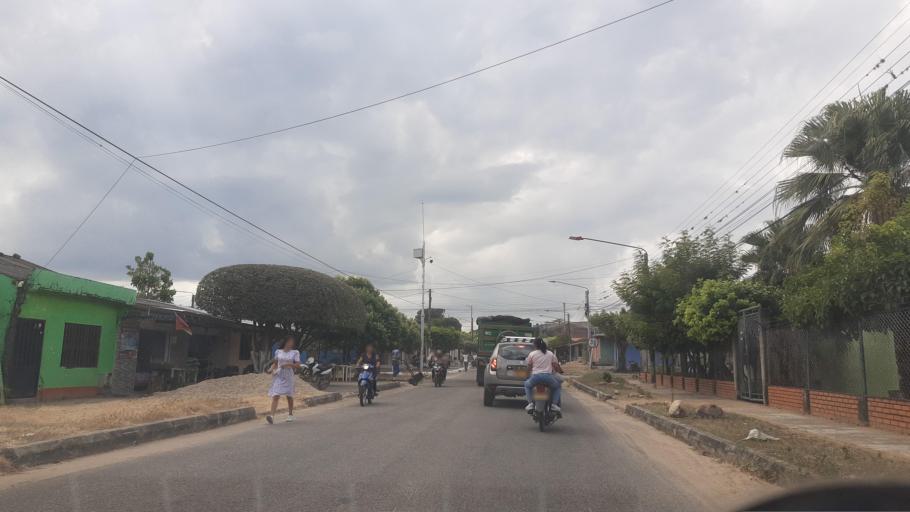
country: CO
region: Casanare
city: Pore
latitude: 5.8832
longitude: -71.8988
